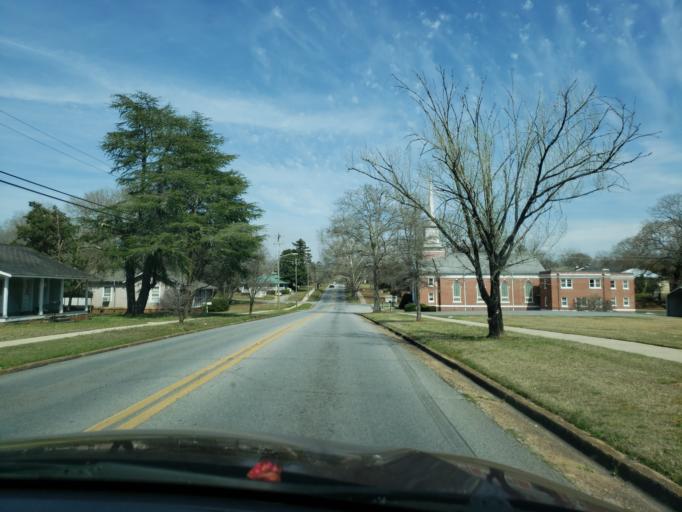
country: US
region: Alabama
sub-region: Elmore County
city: Tallassee
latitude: 32.5370
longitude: -85.8796
